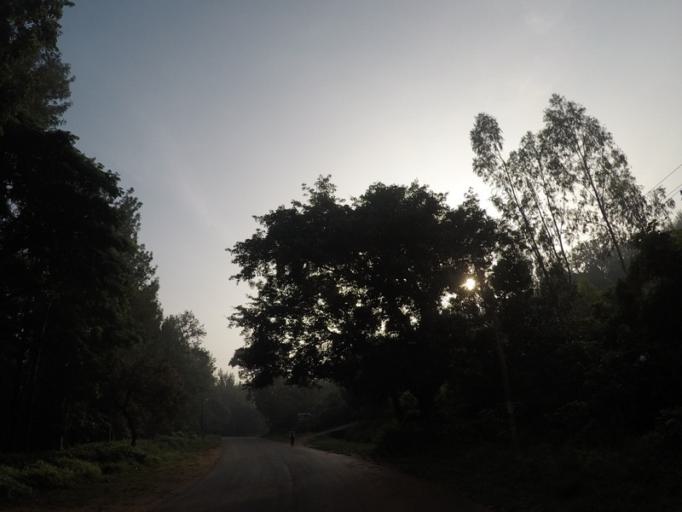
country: IN
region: Karnataka
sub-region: Chikmagalur
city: Chikmagalur
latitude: 13.3923
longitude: 75.7733
